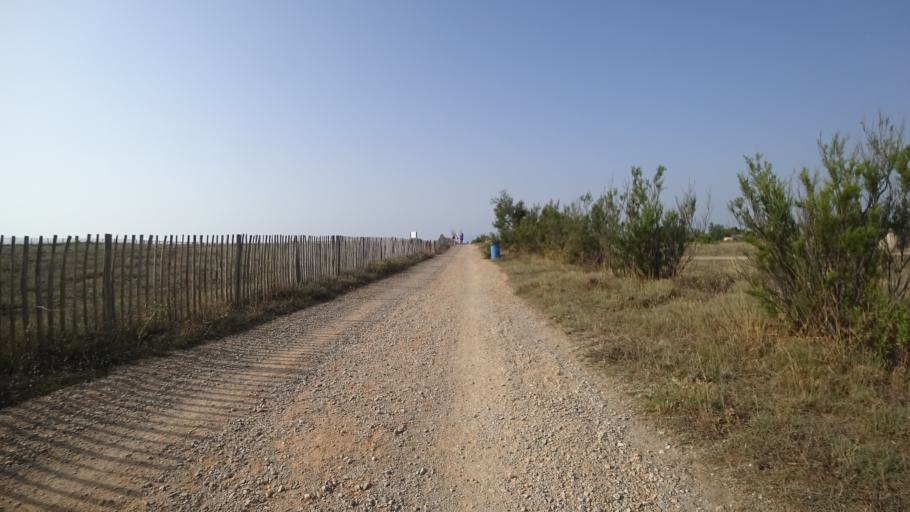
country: FR
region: Languedoc-Roussillon
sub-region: Departement des Pyrenees-Orientales
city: Le Barcares
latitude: 42.7617
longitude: 3.0372
